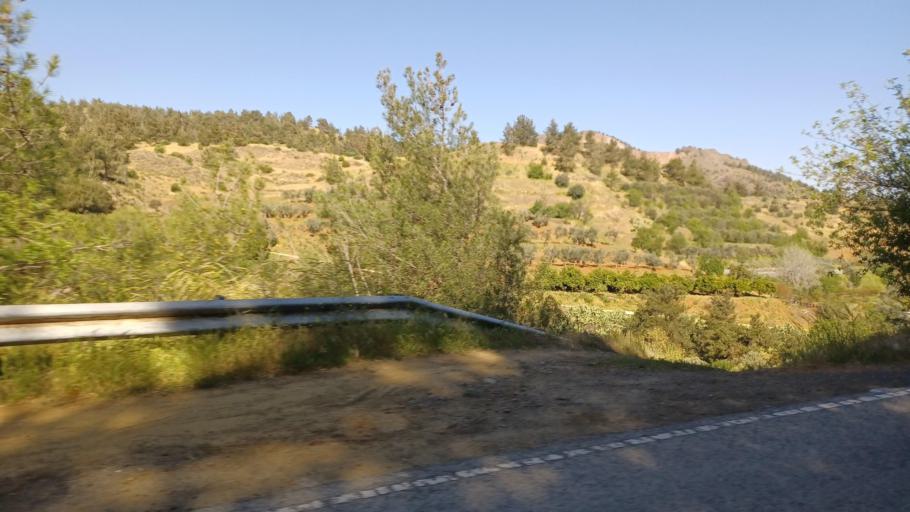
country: CY
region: Limassol
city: Kyperounta
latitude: 35.0250
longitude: 33.0371
